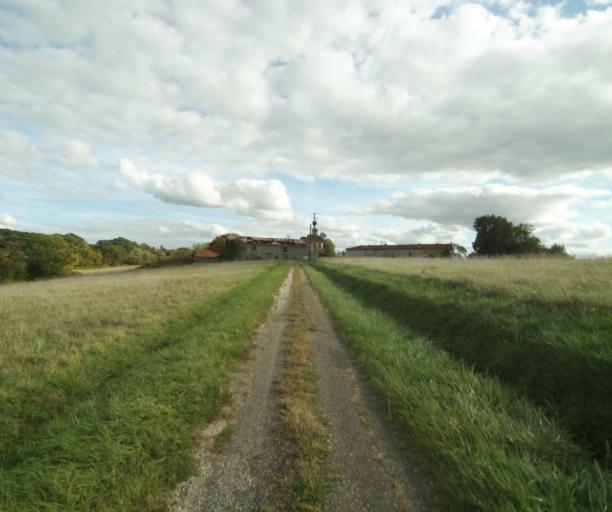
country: FR
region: Midi-Pyrenees
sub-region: Departement du Gers
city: Gondrin
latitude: 43.8709
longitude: 0.2233
